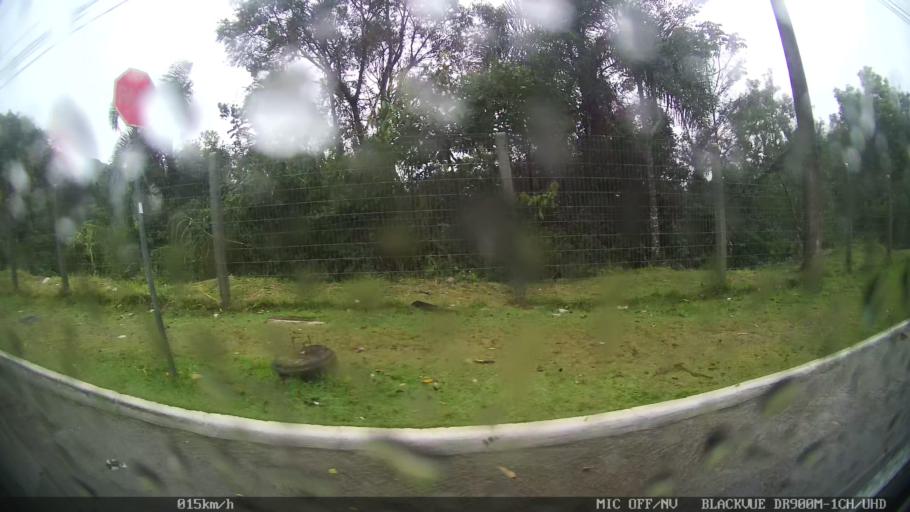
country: BR
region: Santa Catarina
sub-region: Itajai
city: Itajai
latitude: -26.9388
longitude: -48.6409
